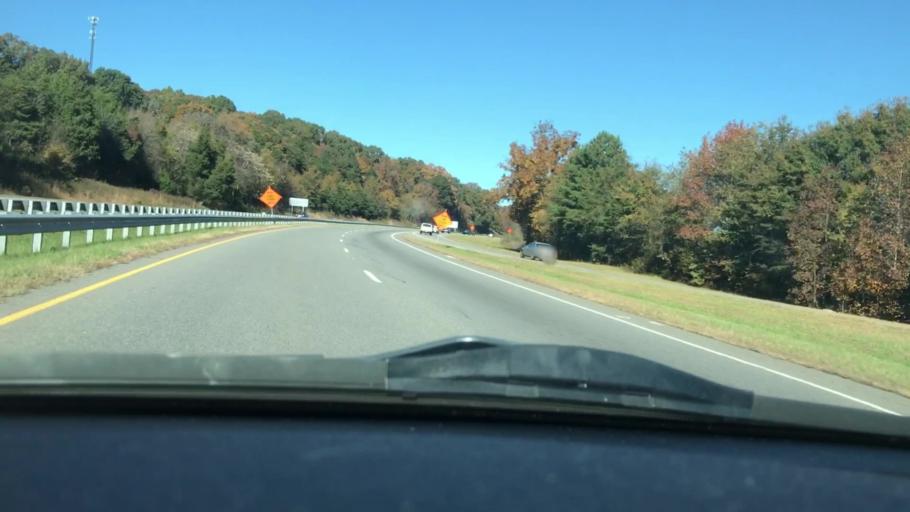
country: US
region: North Carolina
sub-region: Rockingham County
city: Mayodan
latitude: 36.4198
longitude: -79.9378
